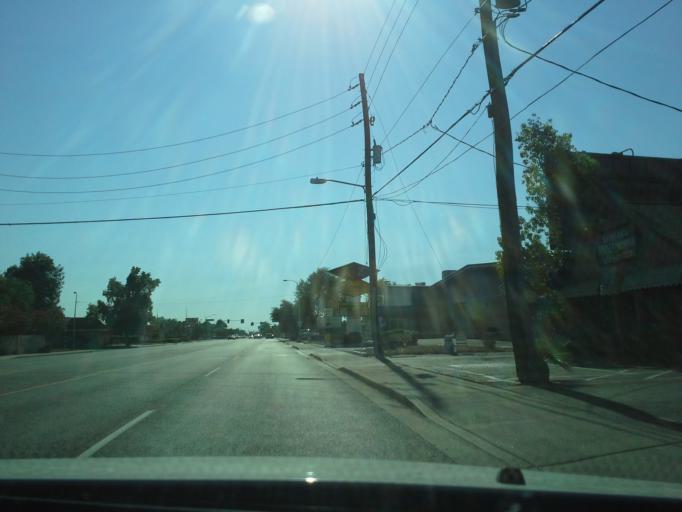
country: US
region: Arizona
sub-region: Maricopa County
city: Paradise Valley
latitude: 33.4951
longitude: -111.9930
